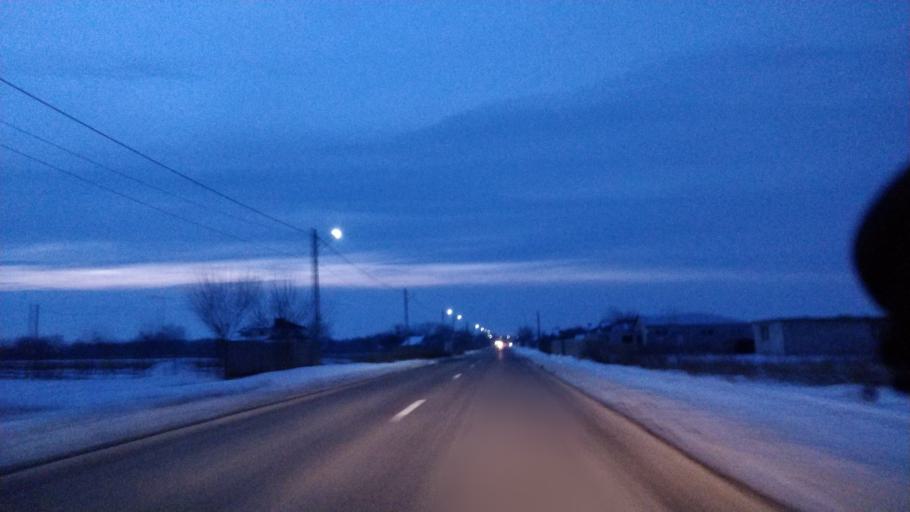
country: RO
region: Vrancea
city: Vulturu de Sus
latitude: 45.6254
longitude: 27.3979
